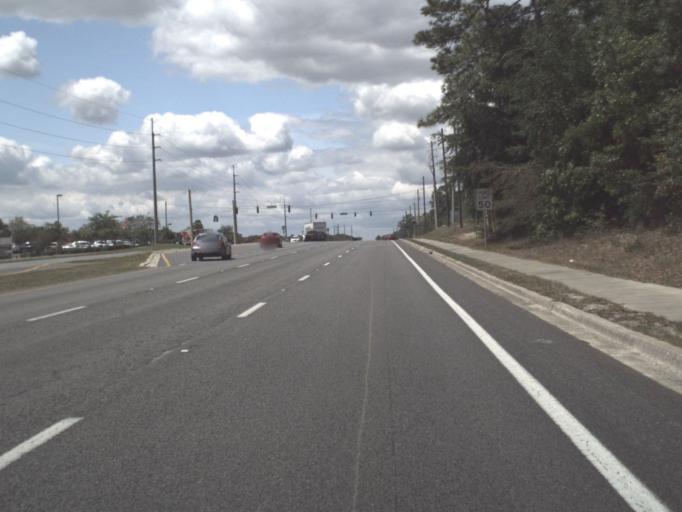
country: US
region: Florida
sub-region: Marion County
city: Dunnellon
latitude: 29.0610
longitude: -82.2761
